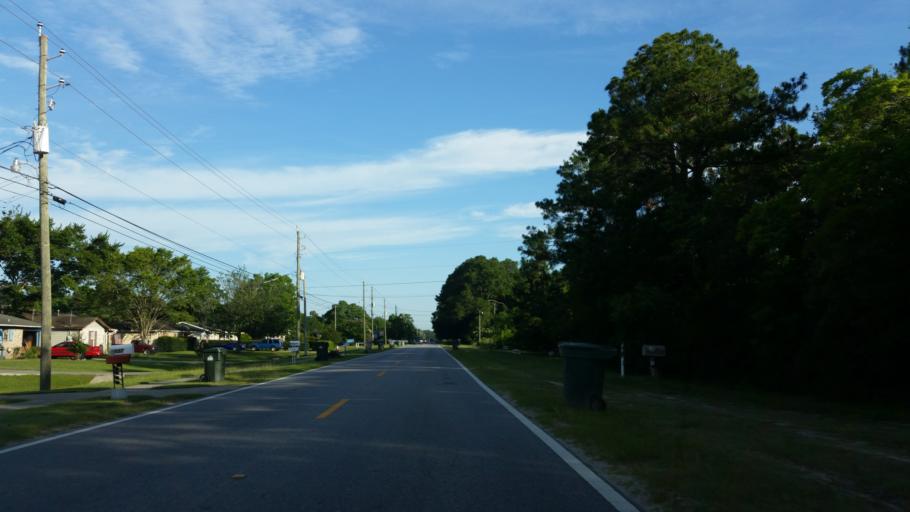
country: US
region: Florida
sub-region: Escambia County
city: Myrtle Grove
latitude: 30.3901
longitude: -87.3615
